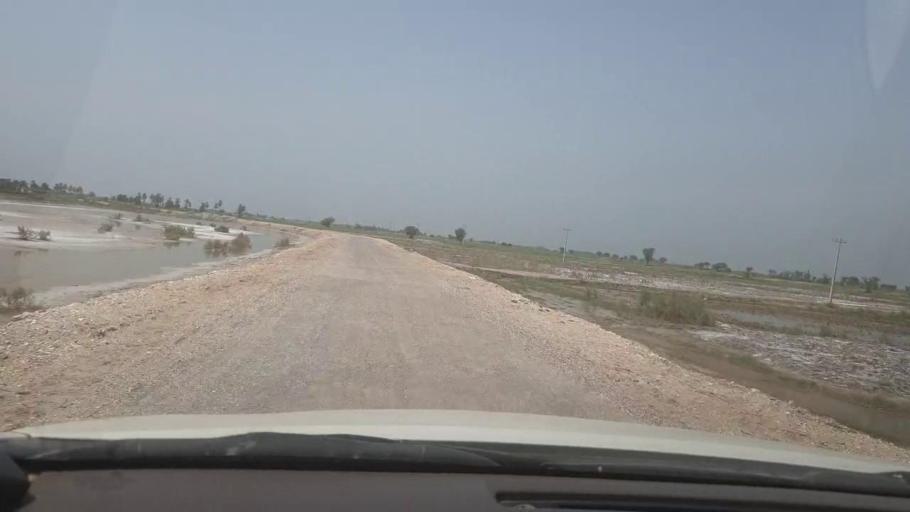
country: PK
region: Sindh
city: Garhi Yasin
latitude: 27.9752
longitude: 68.5477
